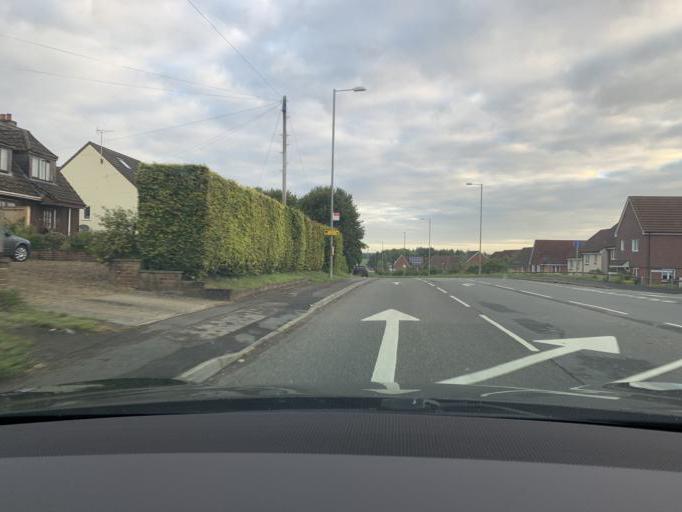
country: GB
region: England
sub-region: Wiltshire
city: Tidworth
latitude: 51.2457
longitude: -1.6652
